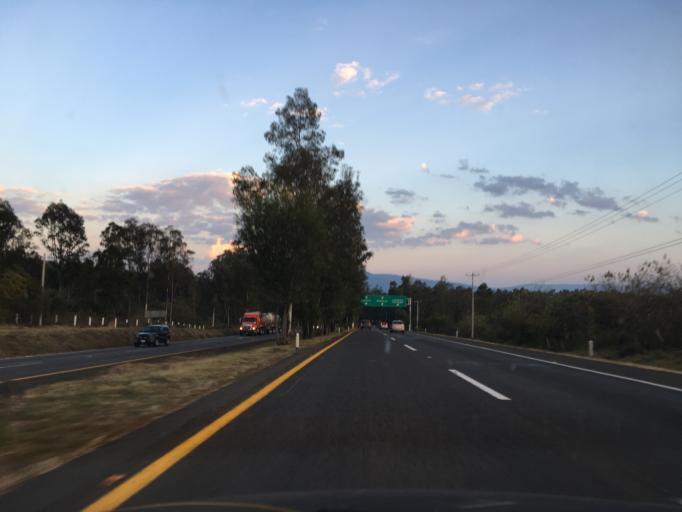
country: MX
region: Michoacan
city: Lagunillas
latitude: 19.5525
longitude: -101.3803
